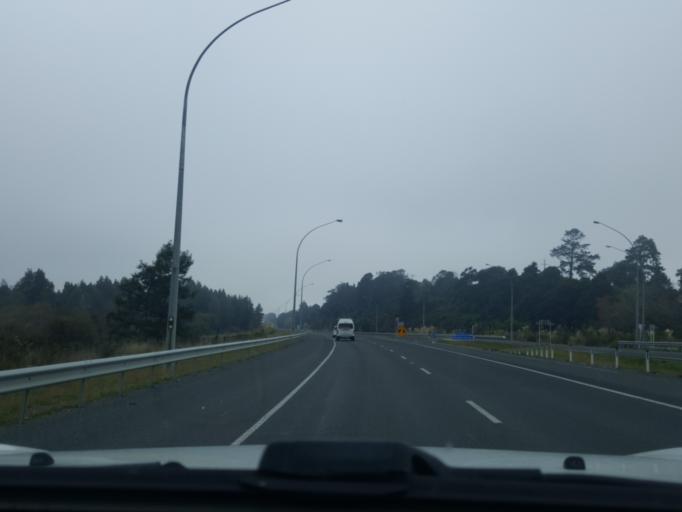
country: NZ
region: Waikato
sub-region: Waikato District
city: Te Kauwhata
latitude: -37.3270
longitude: 175.0657
